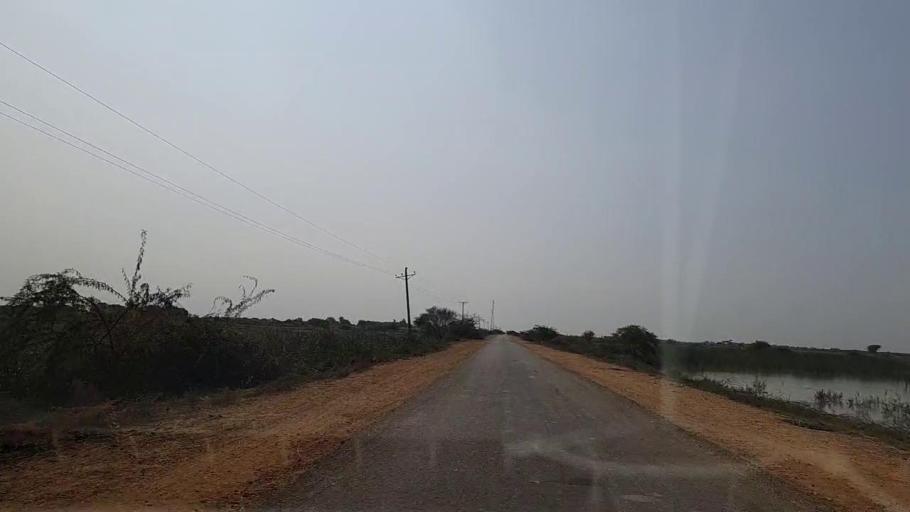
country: PK
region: Sindh
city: Chuhar Jamali
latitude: 24.2931
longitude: 67.9280
